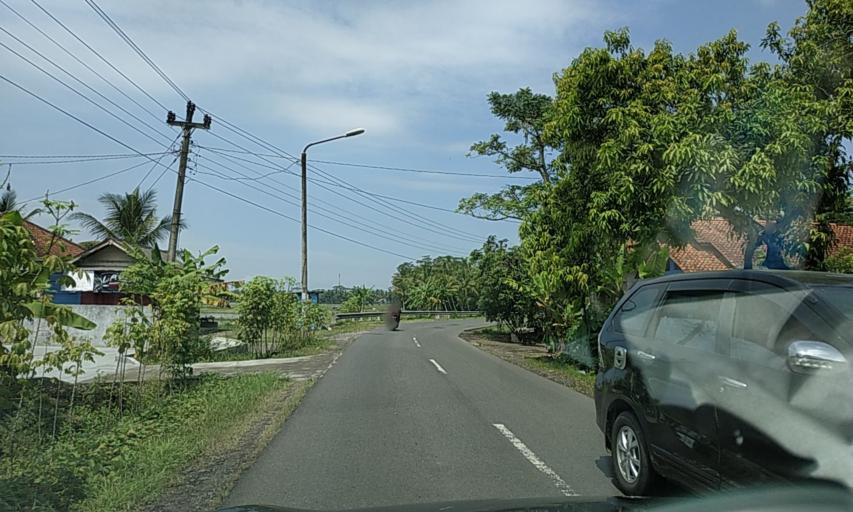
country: ID
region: Central Java
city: Kedungbulu
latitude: -7.5250
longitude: 108.7849
